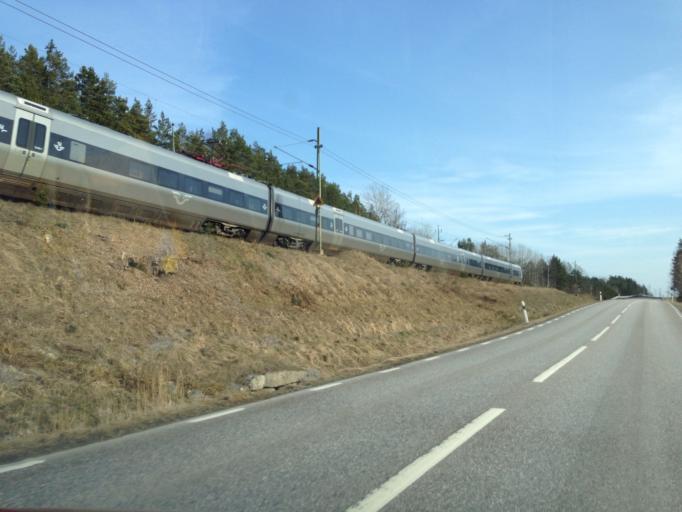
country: SE
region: Soedermanland
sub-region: Flens Kommun
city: Flen
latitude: 59.0622
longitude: 16.6548
